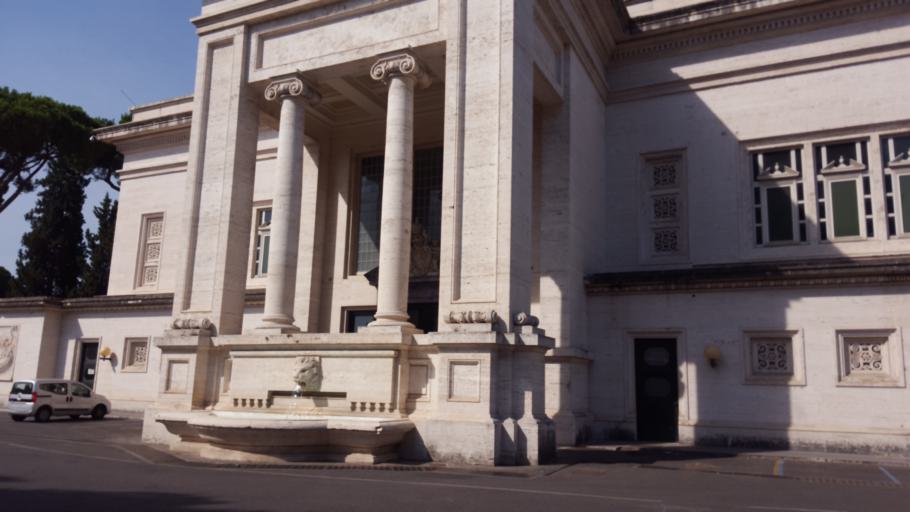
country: VA
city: Vatican City
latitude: 41.9012
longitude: 12.4514
